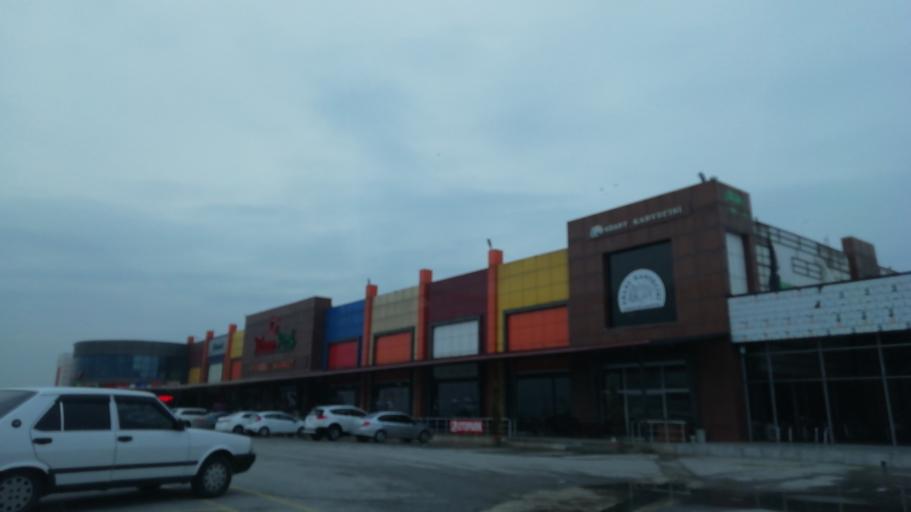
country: TR
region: Duzce
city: Kaynasli
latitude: 40.7915
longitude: 31.2418
